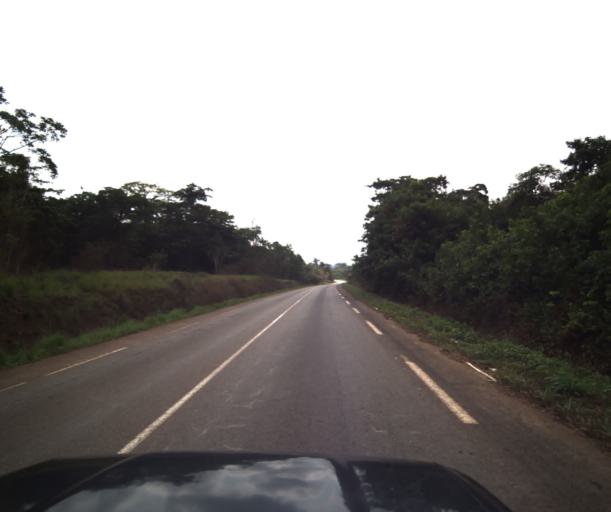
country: CM
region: Centre
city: Eseka
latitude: 3.8574
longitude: 10.5645
